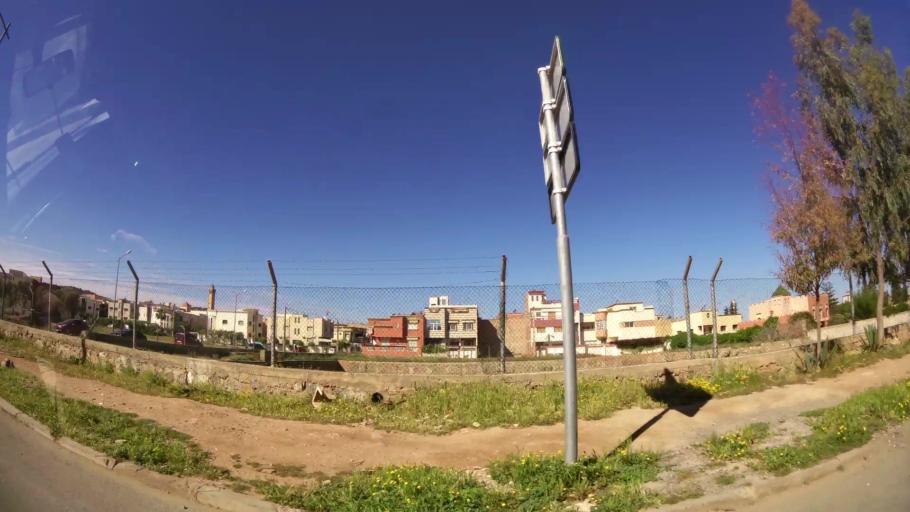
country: MA
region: Oriental
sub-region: Oujda-Angad
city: Oujda
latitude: 34.6561
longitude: -1.8915
